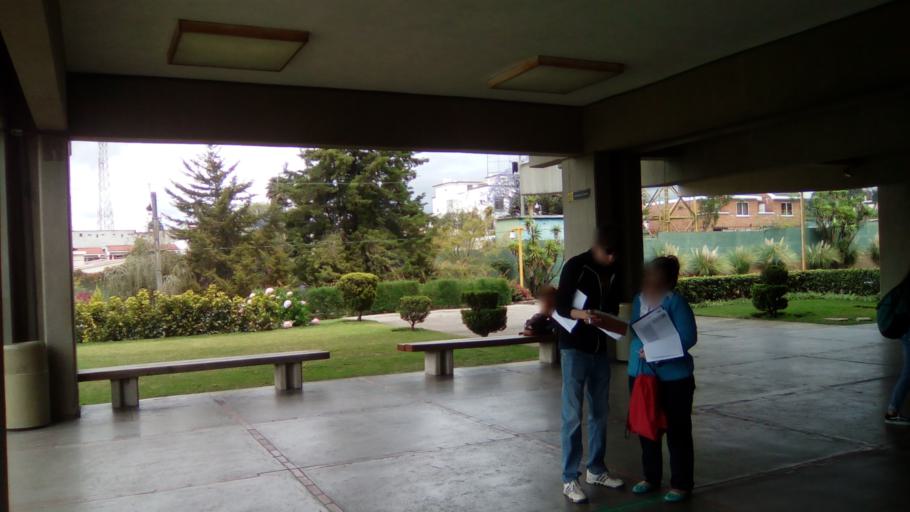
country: GT
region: Guatemala
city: Santa Catarina Pinula
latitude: 14.5956
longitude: -90.4841
